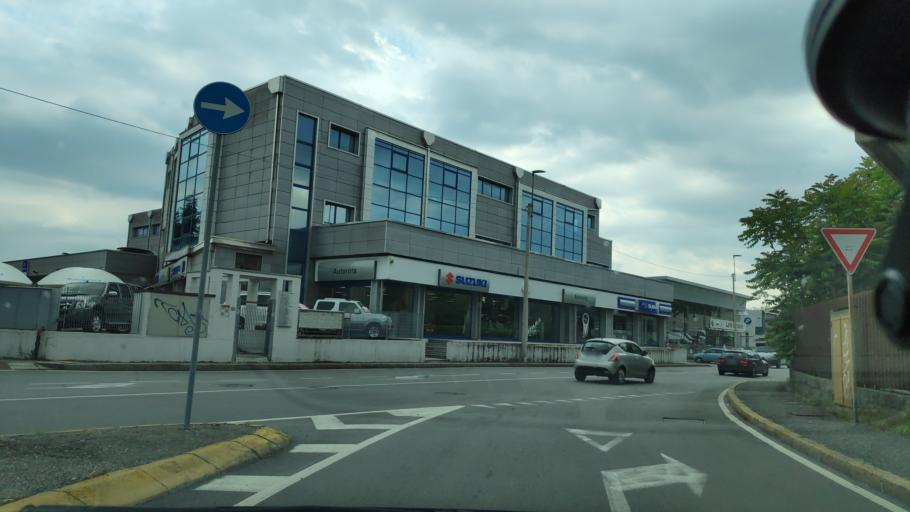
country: IT
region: Lombardy
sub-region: Provincia di Bergamo
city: Orio al Serio
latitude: 45.6782
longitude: 9.6750
